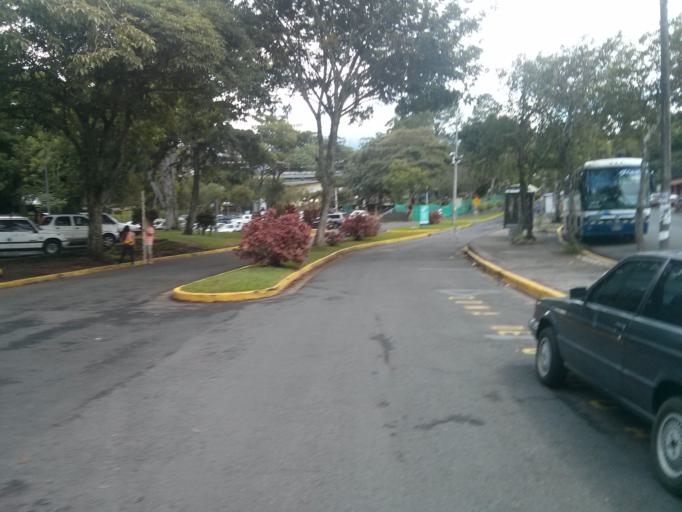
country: CR
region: San Jose
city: San Pedro
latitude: 9.9356
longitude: -84.0502
